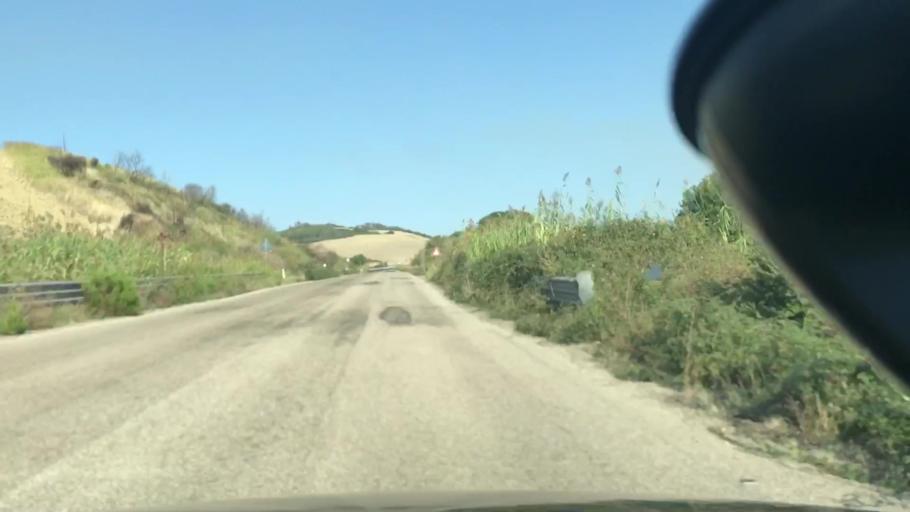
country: IT
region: Basilicate
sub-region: Provincia di Matera
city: Grottole
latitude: 40.6961
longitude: 16.4242
